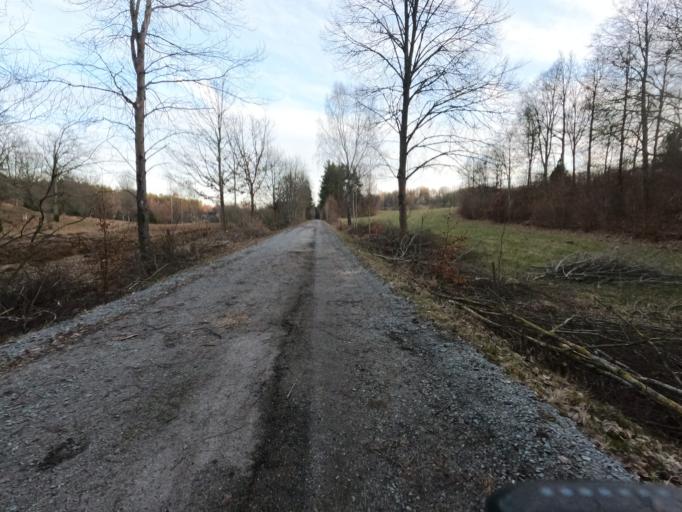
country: SE
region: Blekinge
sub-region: Karlshamns Kommun
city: Svangsta
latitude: 56.2733
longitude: 14.7605
